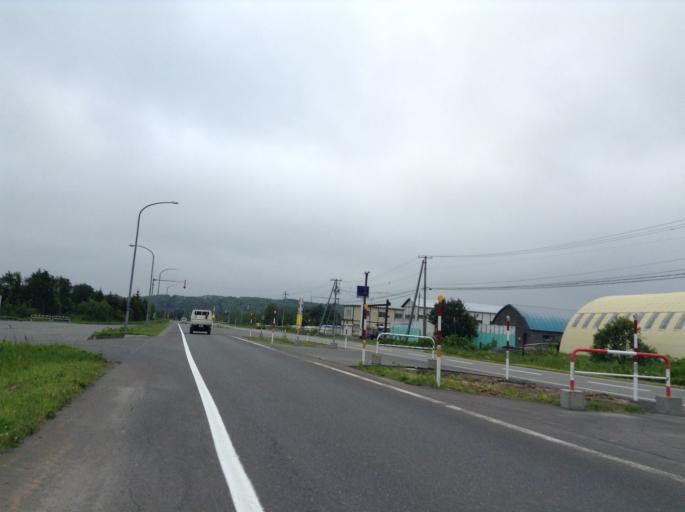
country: JP
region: Hokkaido
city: Wakkanai
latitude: 45.3645
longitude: 141.7291
